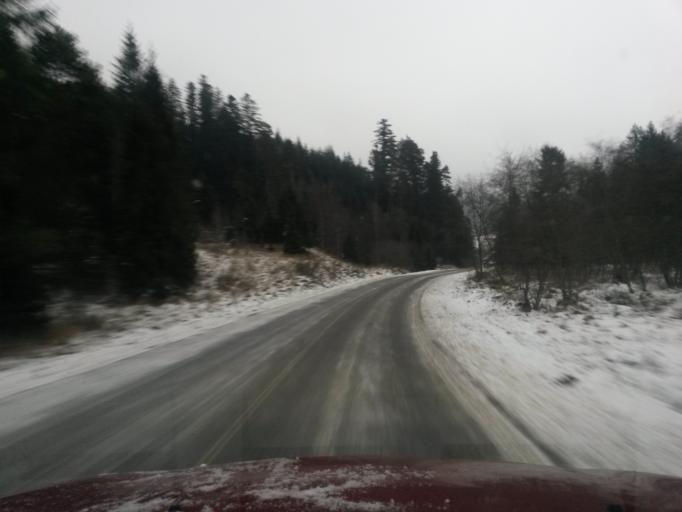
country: SK
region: Kosicky
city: Medzev
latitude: 48.7227
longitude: 20.7124
